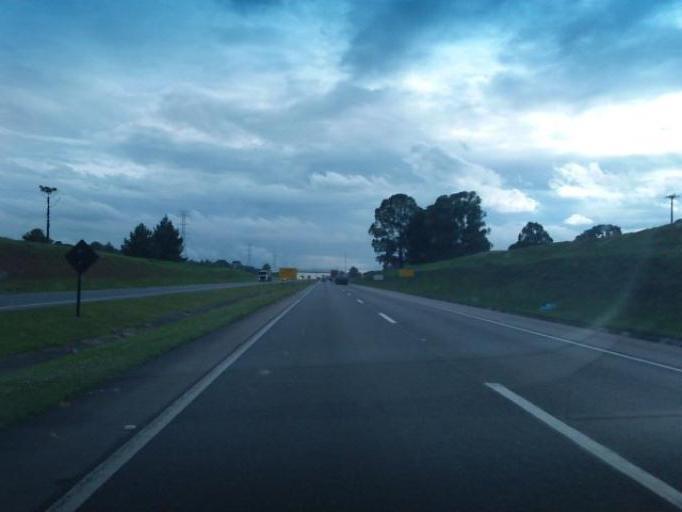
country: BR
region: Parana
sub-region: Piraquara
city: Piraquara
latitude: -25.4868
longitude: -49.1100
